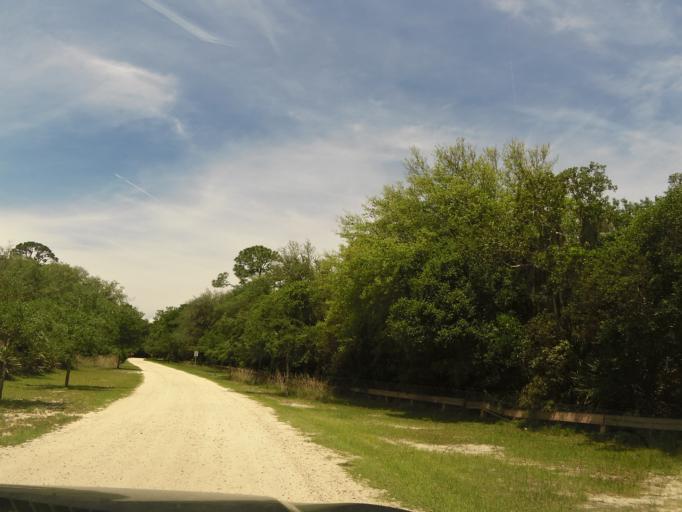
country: US
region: Florida
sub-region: Duval County
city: Atlantic Beach
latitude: 30.4822
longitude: -81.4881
